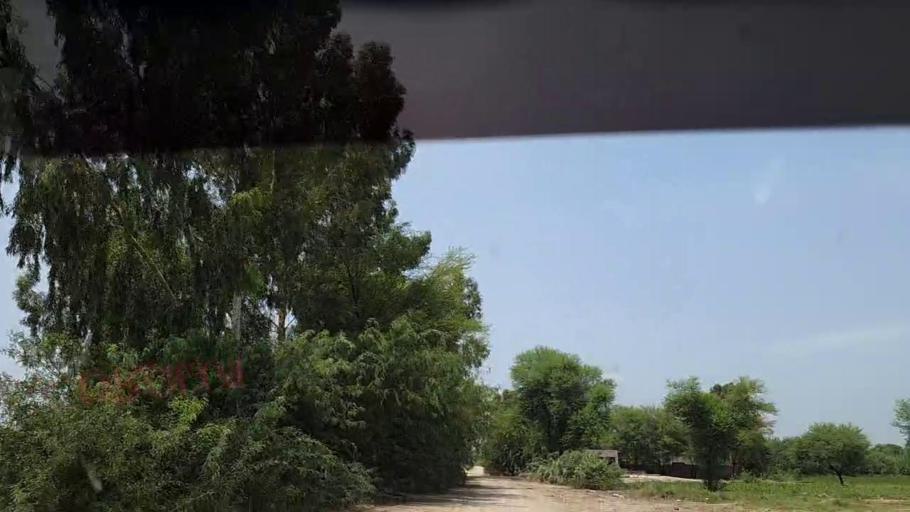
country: PK
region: Sindh
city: Pano Aqil
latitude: 27.9169
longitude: 69.2059
